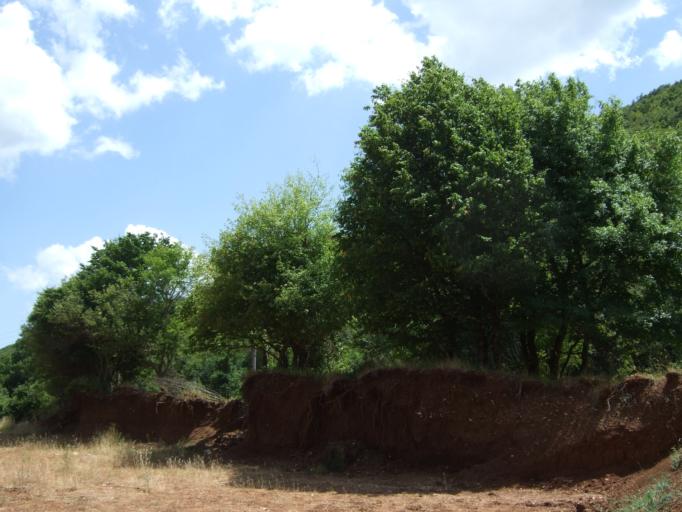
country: GR
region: Epirus
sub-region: Nomos Ioanninon
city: Asprangeloi
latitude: 39.8669
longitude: 20.7291
